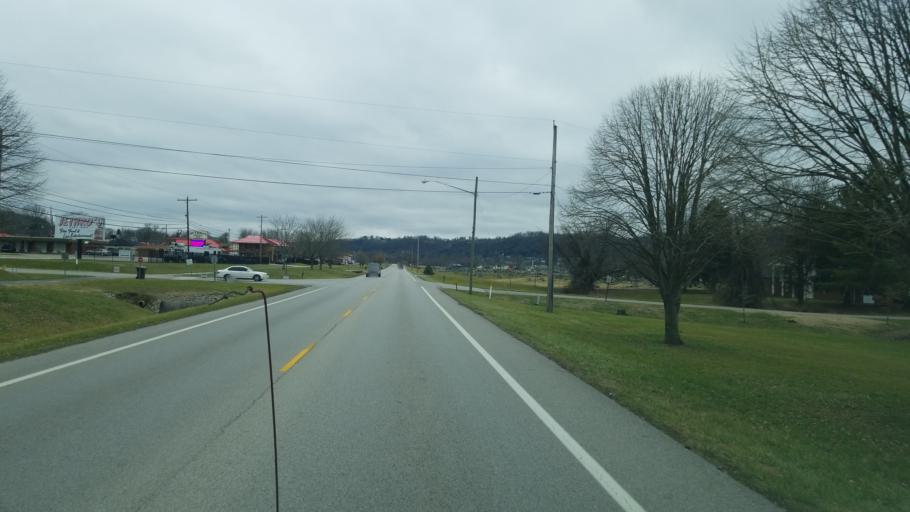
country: US
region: Ohio
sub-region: Brown County
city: Aberdeen
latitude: 38.6744
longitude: -83.7732
